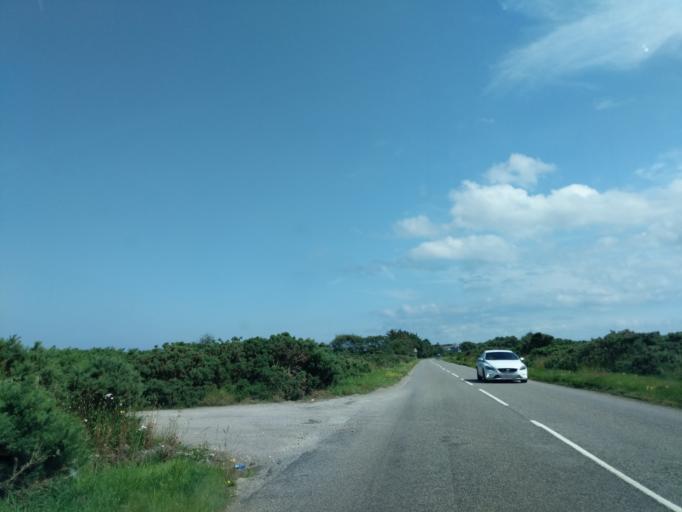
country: GB
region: Scotland
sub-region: Moray
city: Lossiemouth
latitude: 57.7188
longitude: -3.3245
